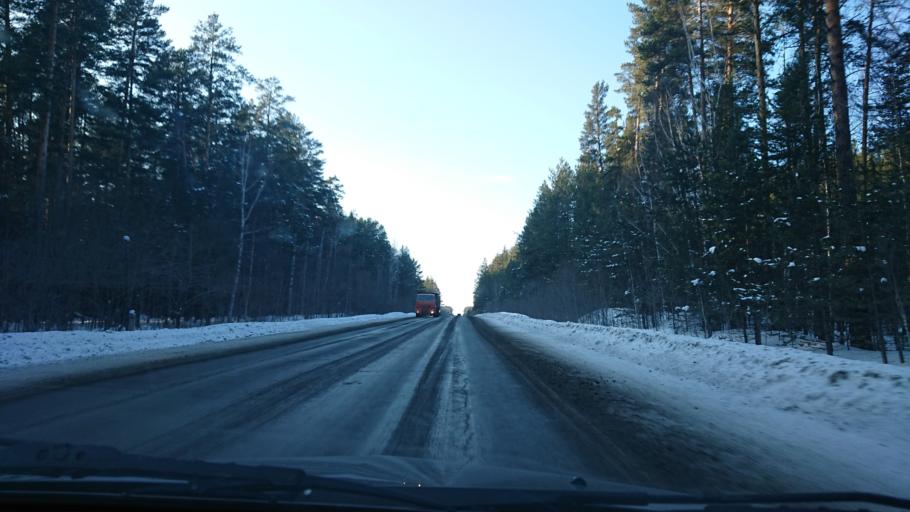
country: RU
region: Sverdlovsk
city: Gornyy Shchit
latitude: 56.6301
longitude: 60.3349
